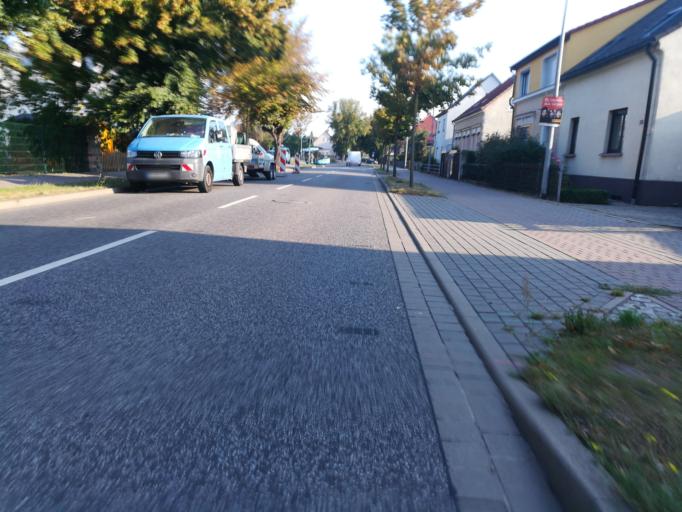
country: DE
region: Saxony-Anhalt
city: Haldensleben I
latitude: 52.2714
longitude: 11.4223
